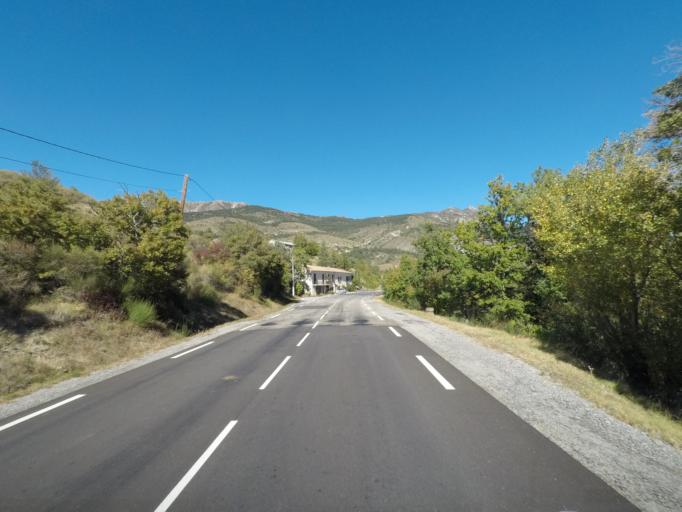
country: FR
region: Provence-Alpes-Cote d'Azur
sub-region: Departement des Hautes-Alpes
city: Serres
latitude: 44.4011
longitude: 5.5058
